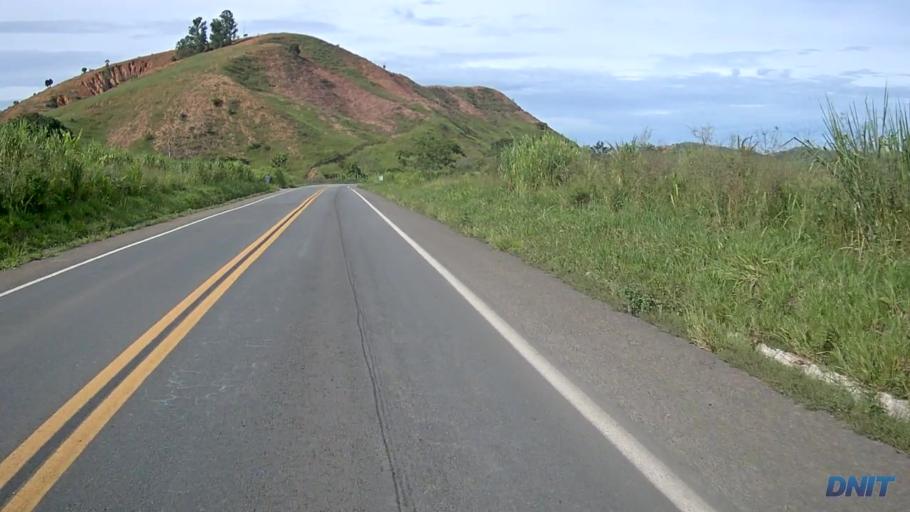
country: BR
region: Minas Gerais
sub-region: Belo Oriente
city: Belo Oriente
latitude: -19.1755
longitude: -42.2549
